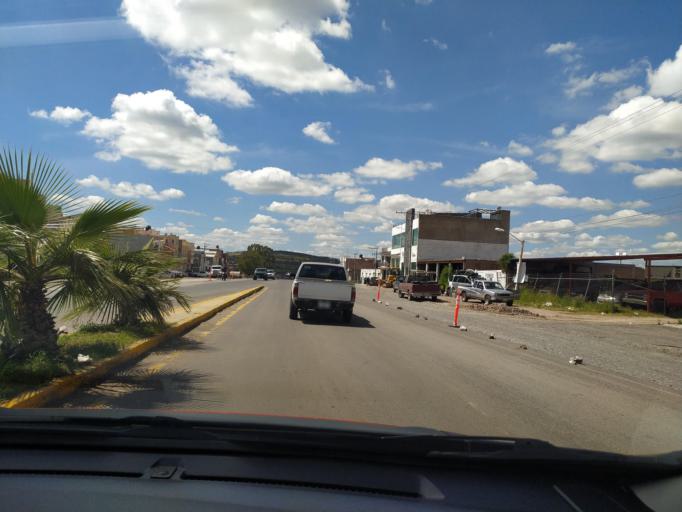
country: MX
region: Jalisco
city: San Miguel el Alto
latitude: 21.0411
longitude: -102.4011
